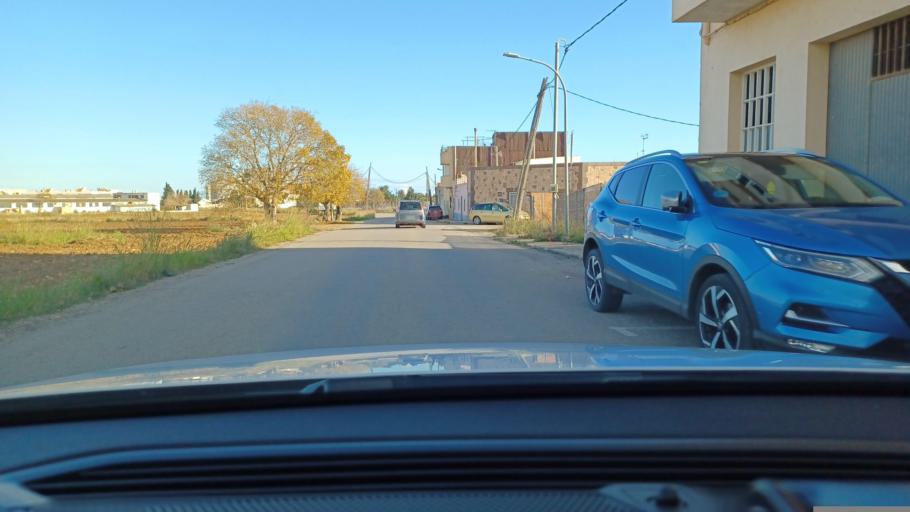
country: ES
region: Catalonia
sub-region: Provincia de Tarragona
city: Amposta
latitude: 40.7007
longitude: 0.5692
